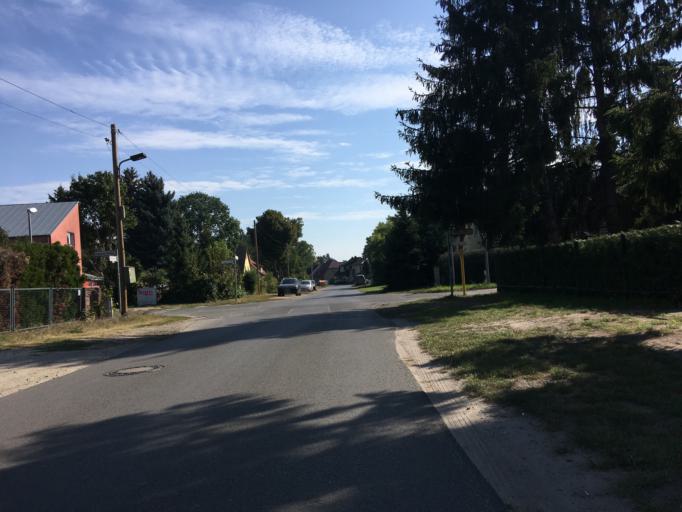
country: DE
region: Berlin
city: Mahlsdorf
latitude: 52.4831
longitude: 13.6070
